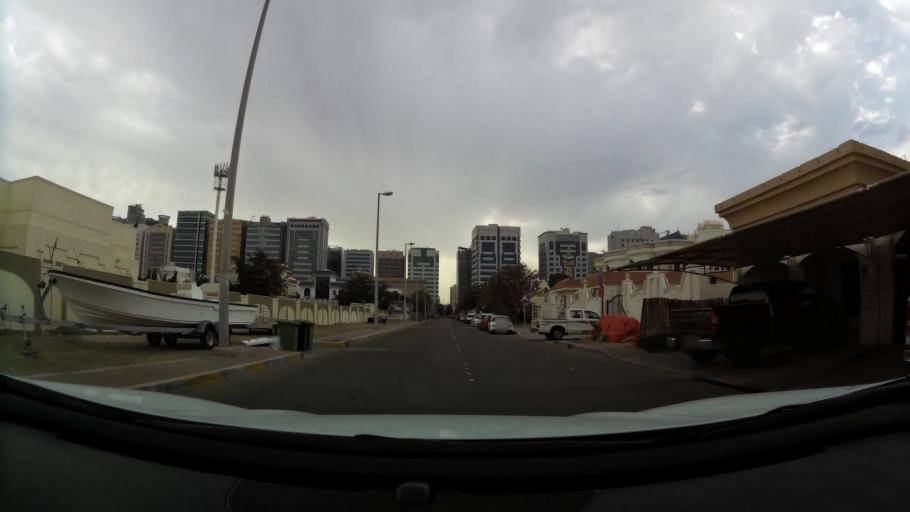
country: AE
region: Abu Dhabi
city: Abu Dhabi
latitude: 24.4782
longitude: 54.3754
